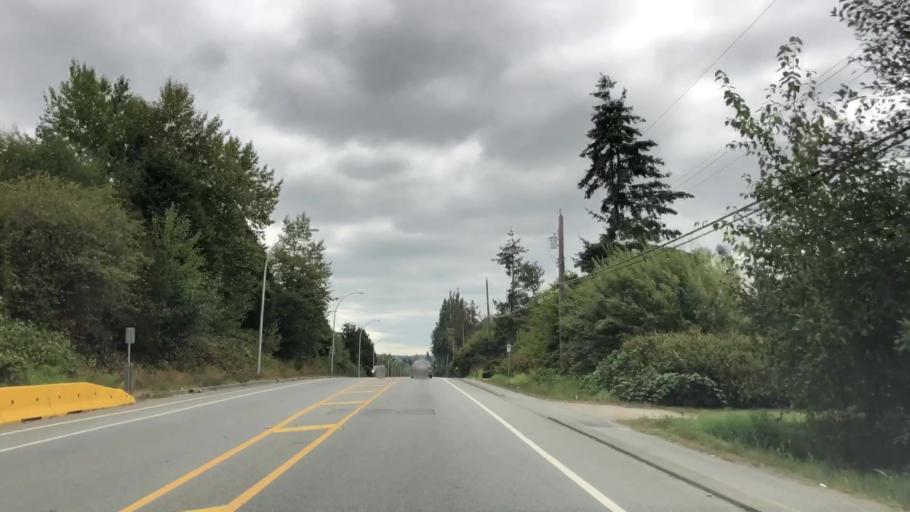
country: CA
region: British Columbia
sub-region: Greater Vancouver Regional District
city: White Rock
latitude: 49.0601
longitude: -122.7712
